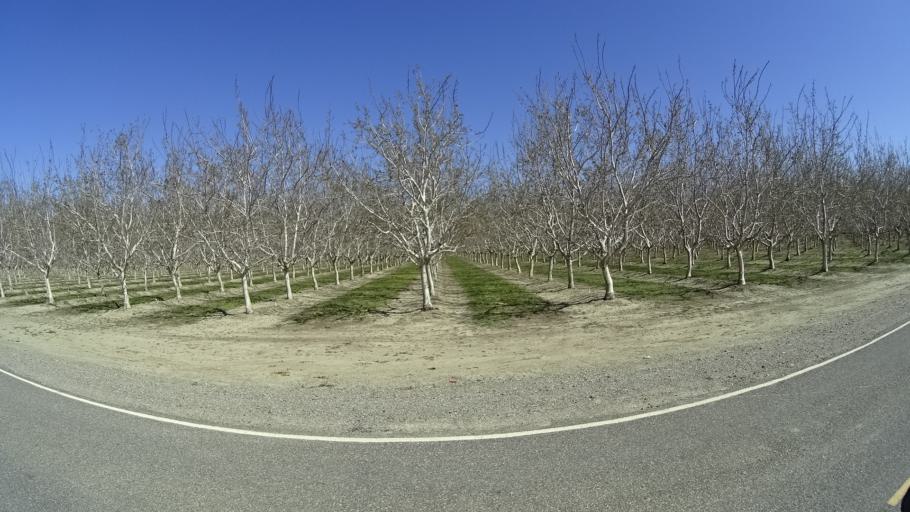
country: US
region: California
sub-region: Glenn County
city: Willows
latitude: 39.6235
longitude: -122.1069
